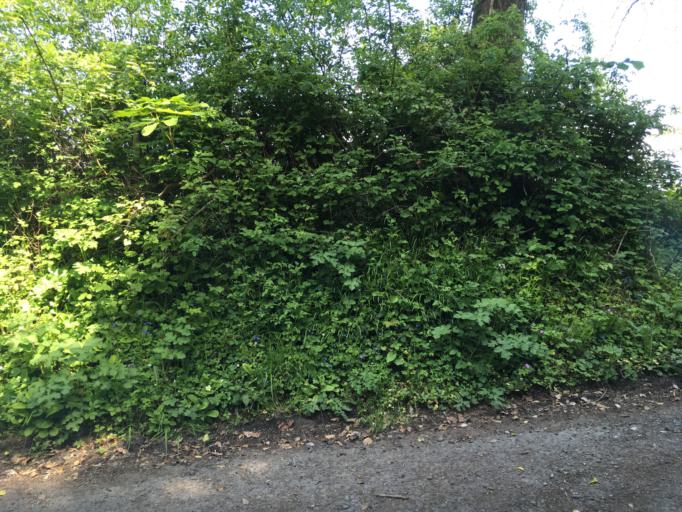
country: GB
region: England
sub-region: Gloucestershire
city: Minchinhampton
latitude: 51.7115
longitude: -2.1898
